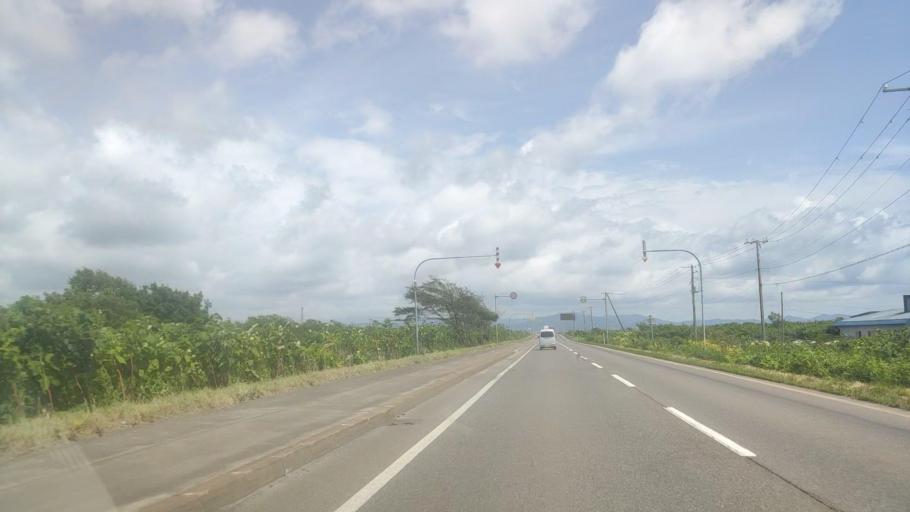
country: JP
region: Hokkaido
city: Niseko Town
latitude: 42.5217
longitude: 140.3846
